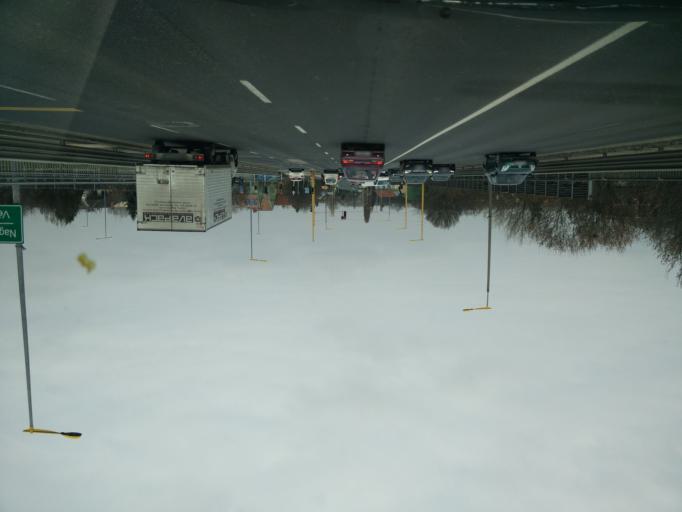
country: HU
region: Gyor-Moson-Sopron
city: Gyor
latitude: 47.6967
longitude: 17.6378
